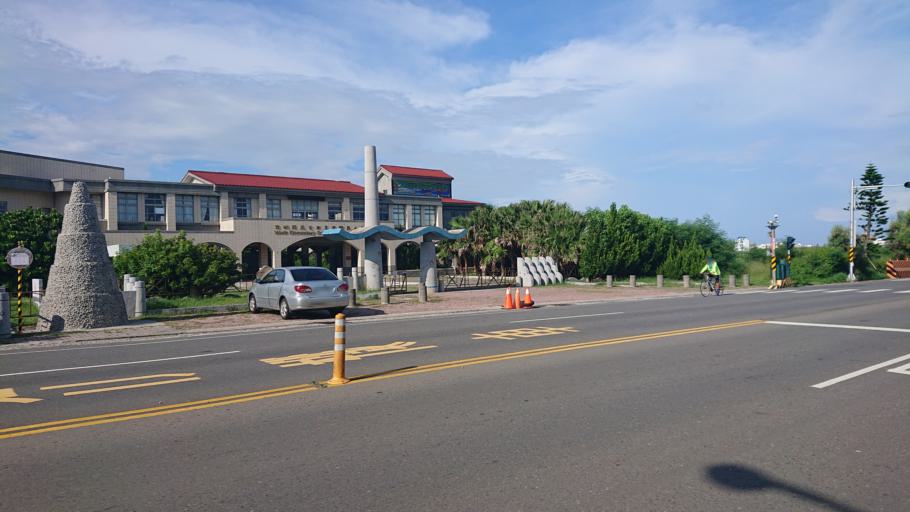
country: TW
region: Taiwan
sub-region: Penghu
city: Ma-kung
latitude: 23.5272
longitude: 119.5904
